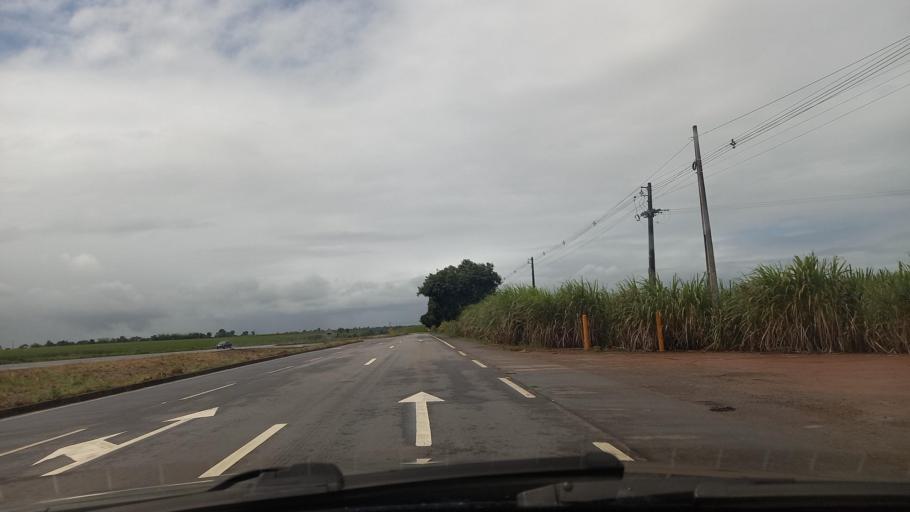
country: BR
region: Alagoas
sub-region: Campo Alegre
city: Campo Alegre
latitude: -9.8231
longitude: -36.2364
